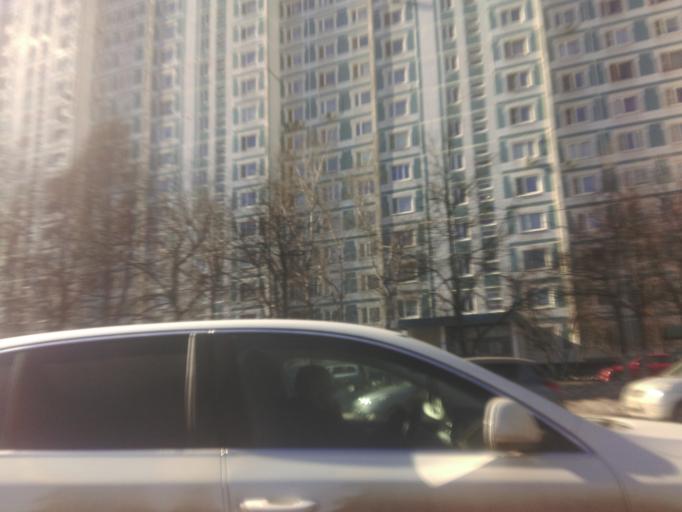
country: RU
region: Moscow
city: Tyoply Stan
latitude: 55.6289
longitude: 37.4845
